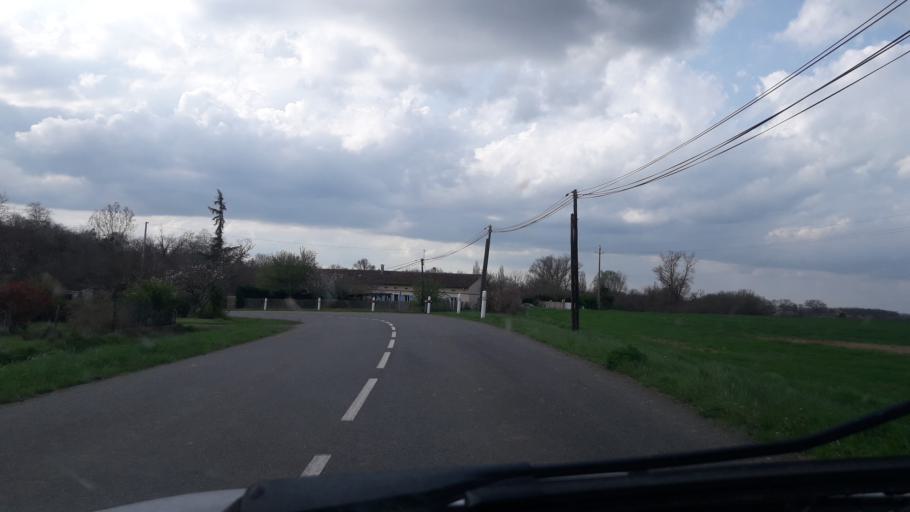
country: FR
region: Midi-Pyrenees
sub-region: Departement de la Haute-Garonne
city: Rieux-Volvestre
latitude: 43.2628
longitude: 1.2203
